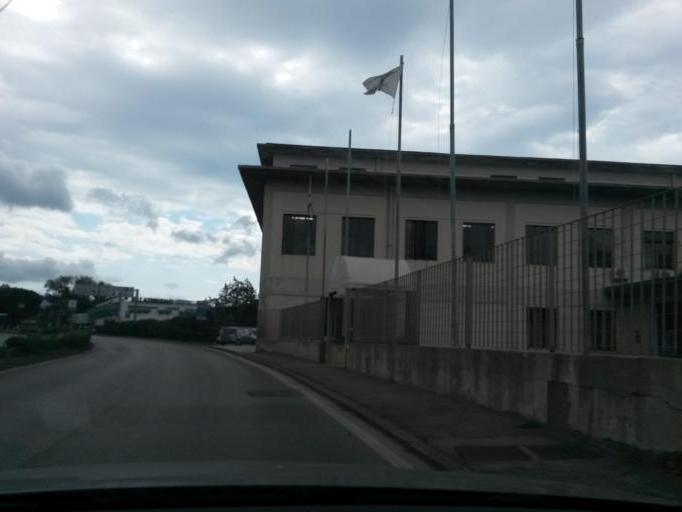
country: IT
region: Tuscany
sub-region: Provincia di Livorno
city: Portoferraio
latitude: 42.8106
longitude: 10.3125
